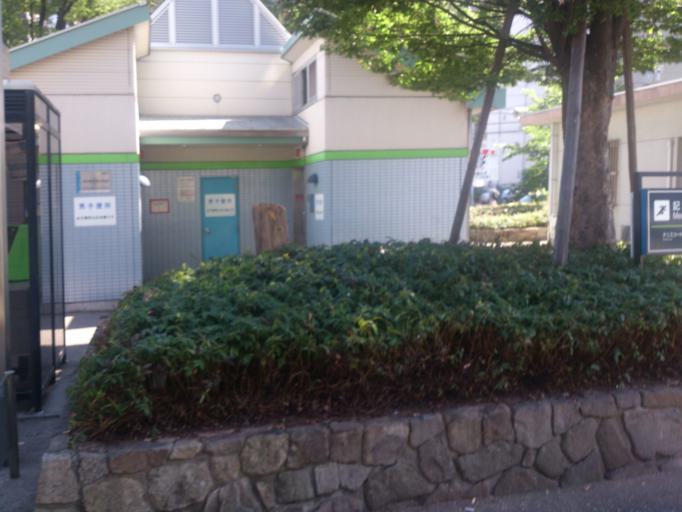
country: JP
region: Hyogo
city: Amagasaki
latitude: 34.7315
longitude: 135.4312
